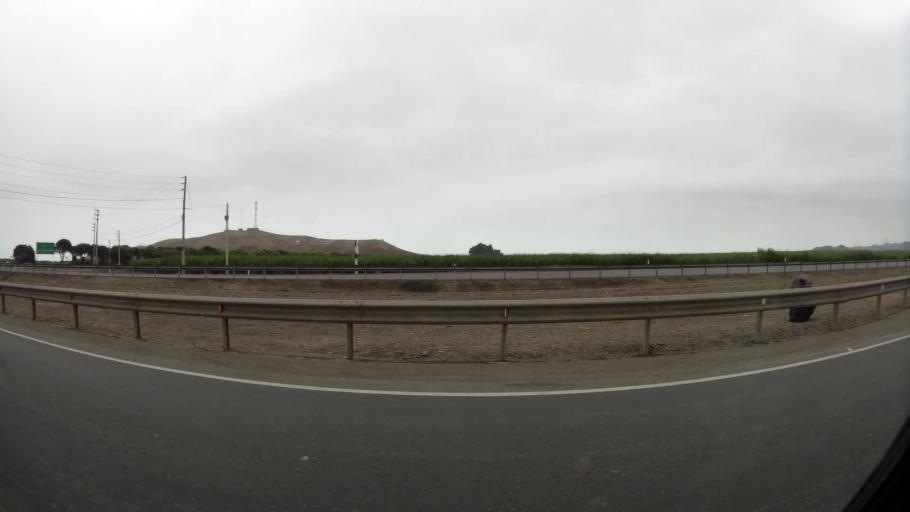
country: PE
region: Lima
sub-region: Barranca
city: Pativilca
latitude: -10.6704
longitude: -77.7939
